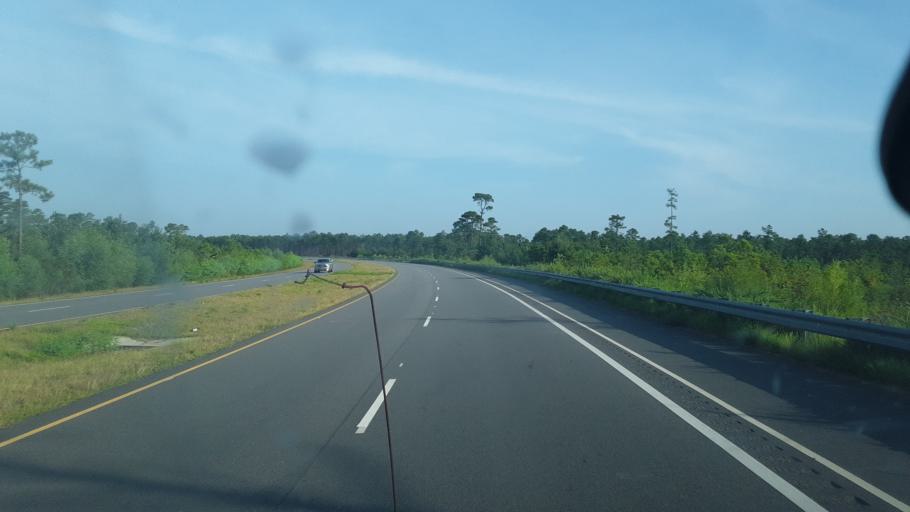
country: US
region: South Carolina
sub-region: Horry County
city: Forestbrook
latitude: 33.7991
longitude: -78.8831
